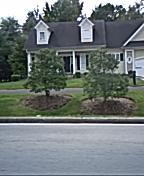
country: US
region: Kentucky
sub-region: Jefferson County
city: Hurstbourne
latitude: 38.2459
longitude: -85.5705
